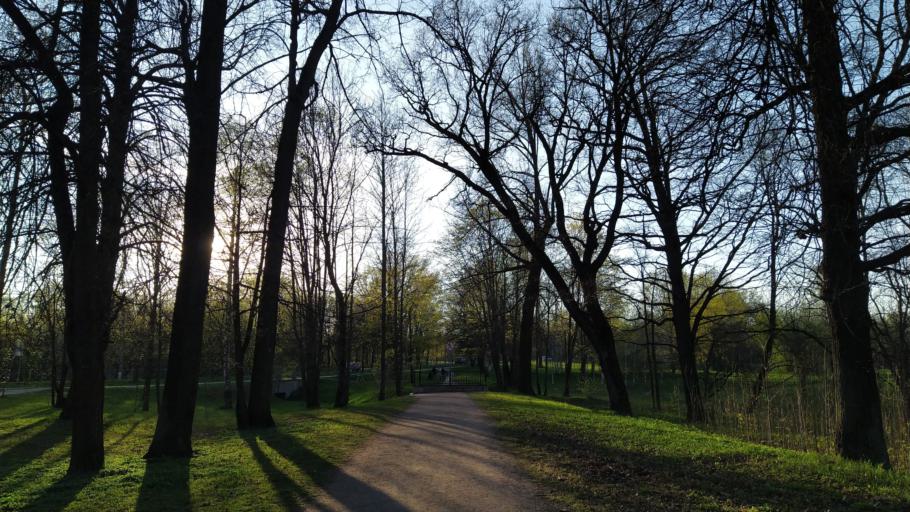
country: RU
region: St.-Petersburg
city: Pavlovsk
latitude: 59.7009
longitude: 30.4235
